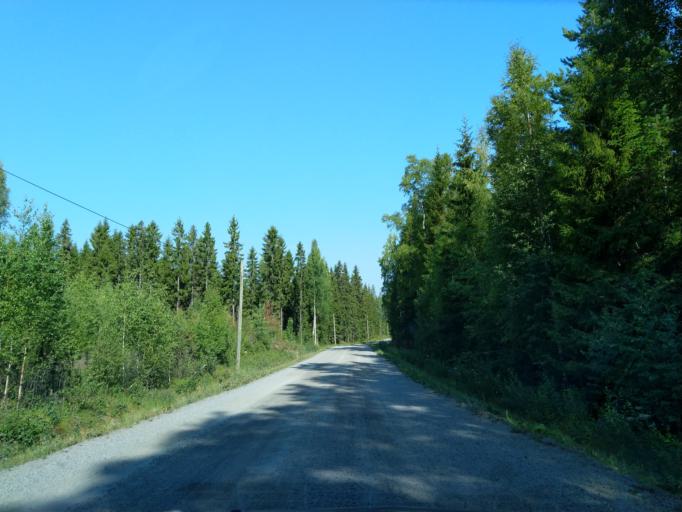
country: FI
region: Satakunta
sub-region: Pori
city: Laengelmaeki
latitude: 61.7262
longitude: 22.1881
